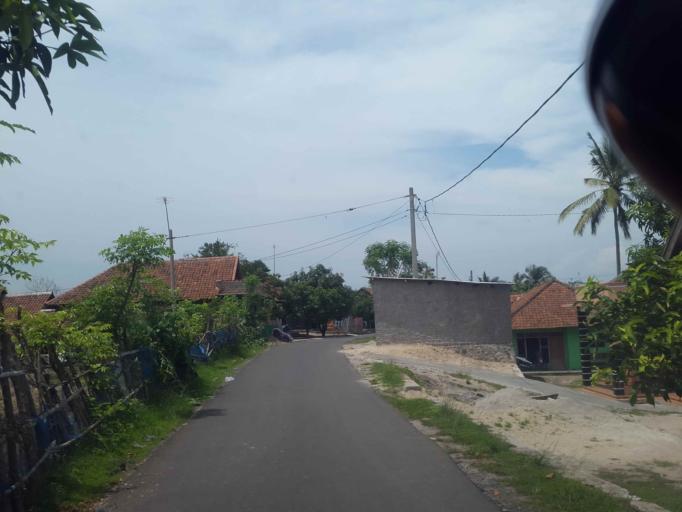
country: ID
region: Banten
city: Curug
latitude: -6.0395
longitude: 105.9964
